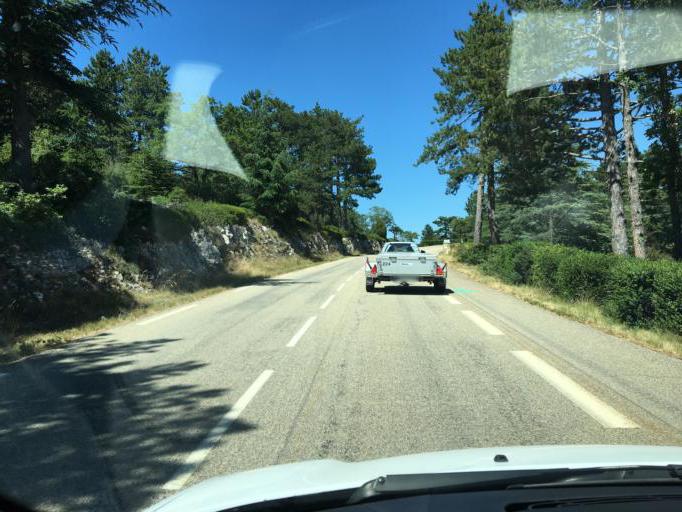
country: FR
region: Provence-Alpes-Cote d'Azur
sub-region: Departement du Vaucluse
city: Bedoin
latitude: 44.1685
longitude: 5.1954
